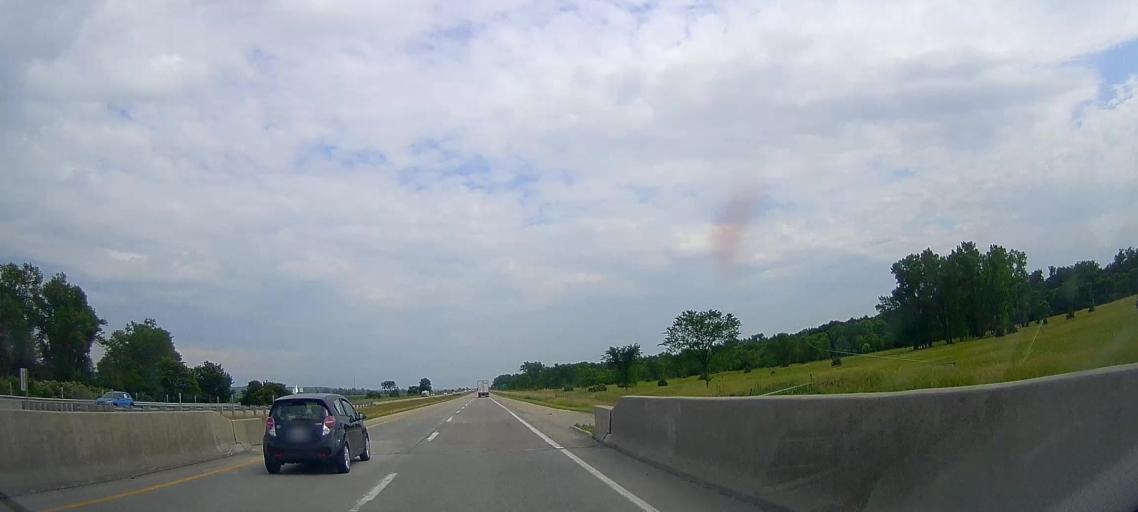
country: US
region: Nebraska
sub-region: Burt County
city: Tekamah
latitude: 41.8203
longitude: -96.0721
